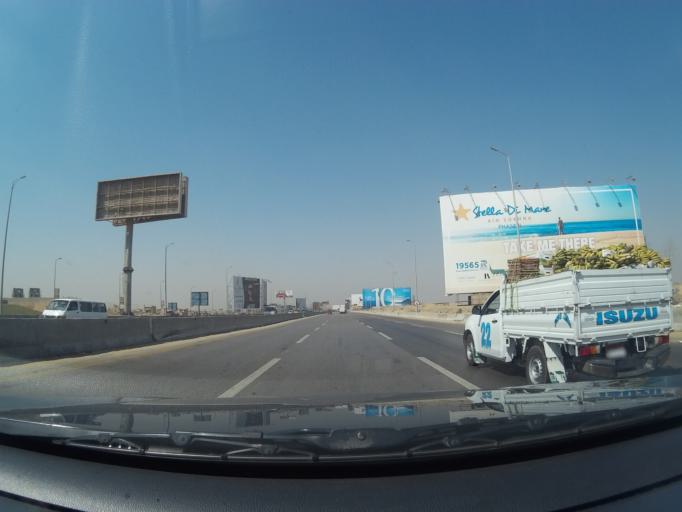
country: EG
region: Muhafazat al Qahirah
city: Cairo
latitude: 29.9963
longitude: 31.3906
